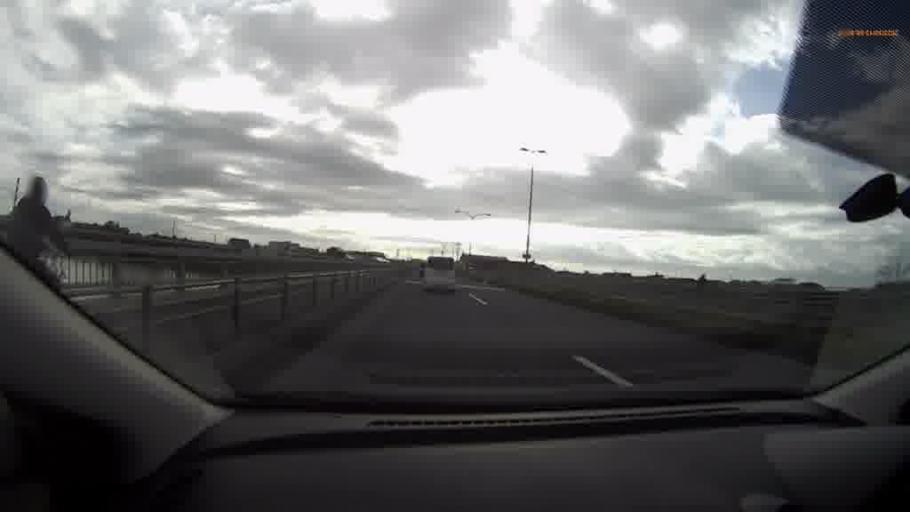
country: JP
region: Hokkaido
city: Kushiro
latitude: 43.0112
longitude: 144.2674
